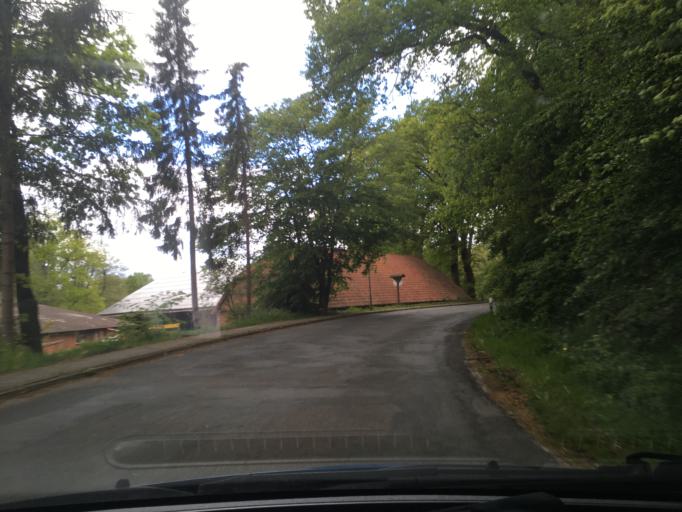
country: DE
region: Lower Saxony
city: Suderburg
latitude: 52.8601
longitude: 10.4200
